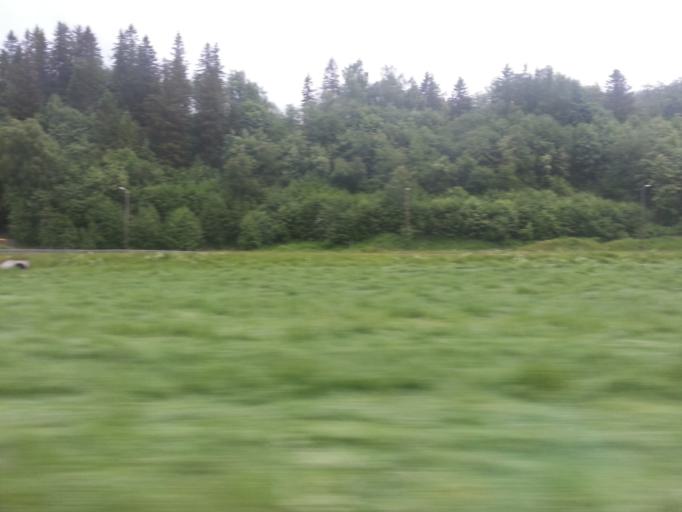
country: NO
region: Sor-Trondelag
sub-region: Melhus
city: Lundamo
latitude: 63.1285
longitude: 10.2434
